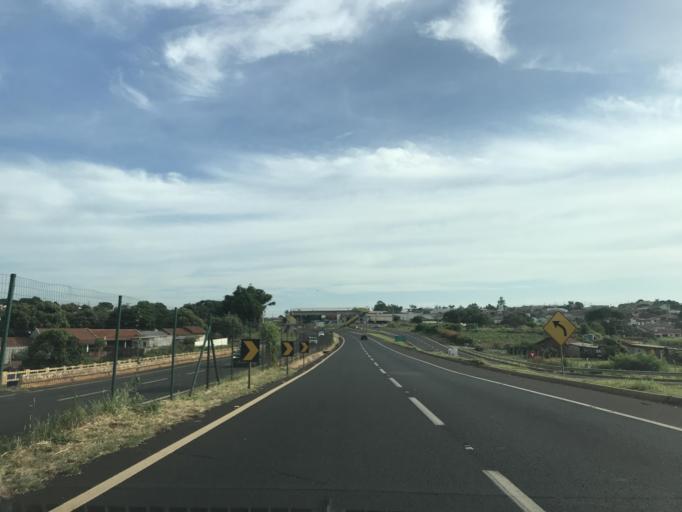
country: BR
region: Parana
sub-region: Mandaguacu
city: Mandaguacu
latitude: -23.3486
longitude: -52.0906
